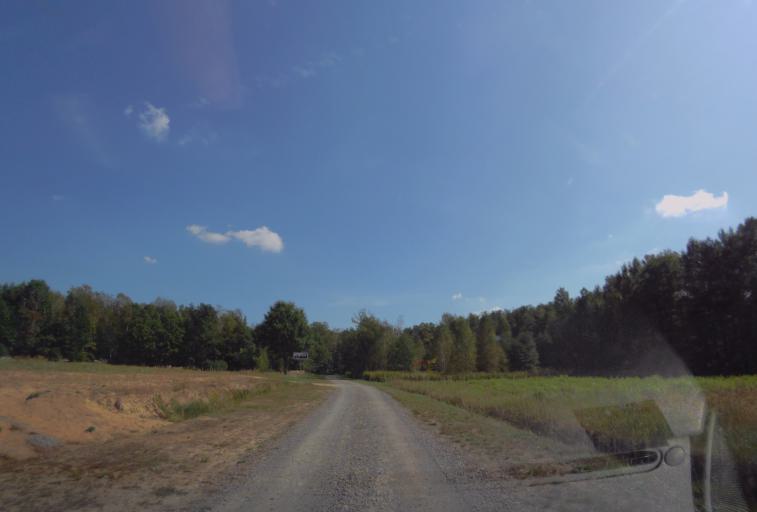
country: PL
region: Subcarpathian Voivodeship
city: Nowa Sarzyna
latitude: 50.2994
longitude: 22.3140
